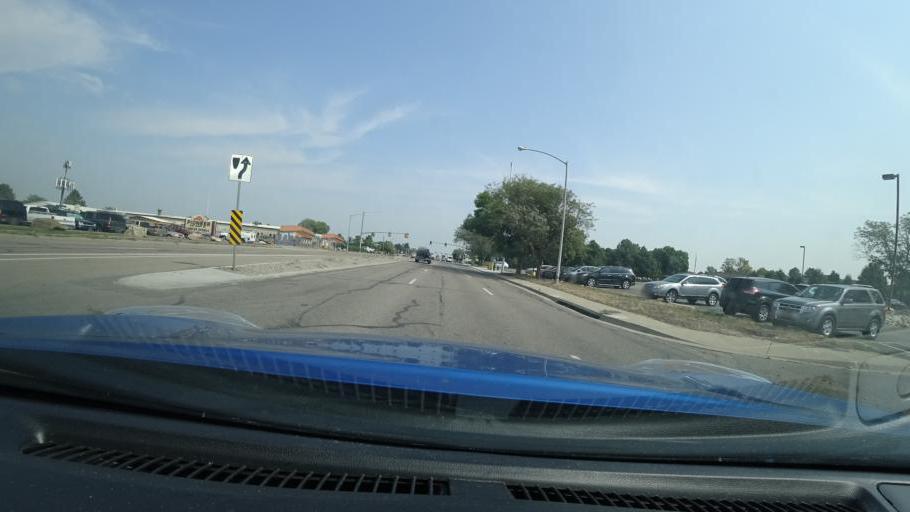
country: US
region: Colorado
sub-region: Adams County
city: Aurora
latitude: 39.7228
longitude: -104.7911
